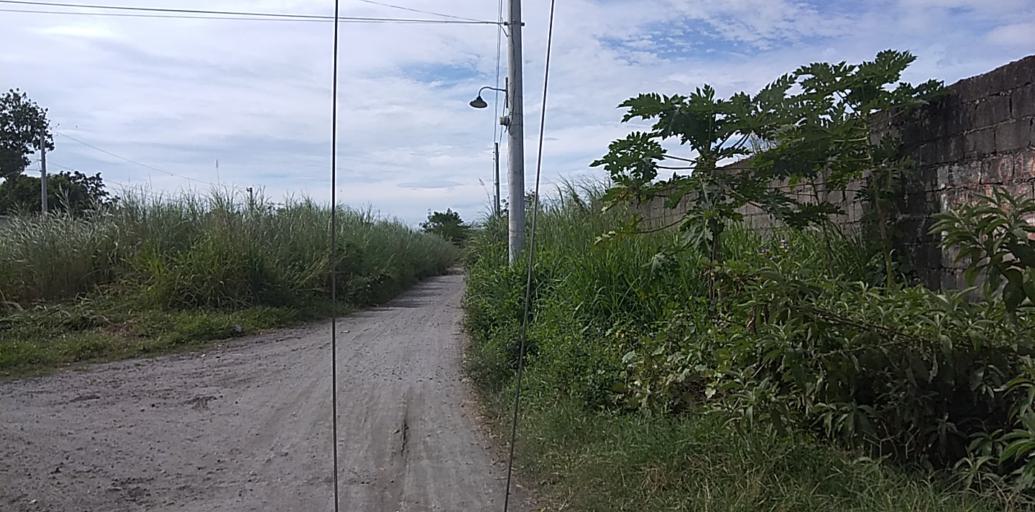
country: PH
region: Central Luzon
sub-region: Province of Pampanga
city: Manibaug Pasig
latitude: 15.1284
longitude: 120.5549
